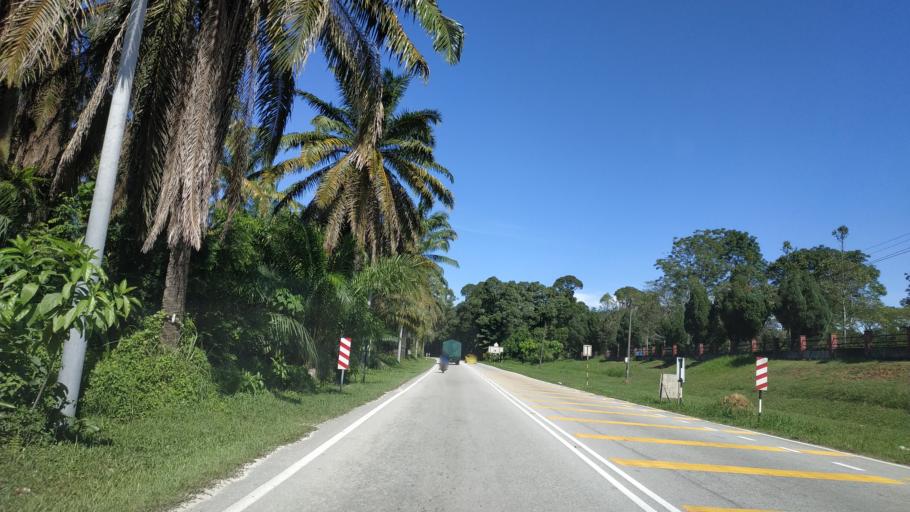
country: MY
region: Kedah
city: Kulim
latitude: 5.3183
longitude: 100.5395
